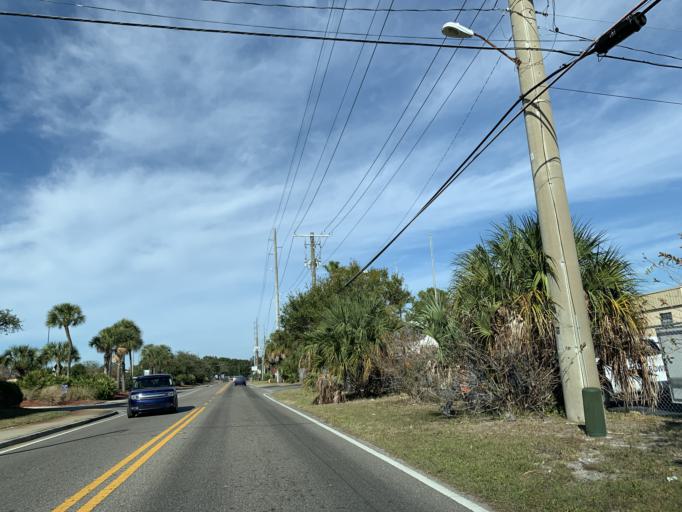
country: US
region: Florida
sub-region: Hillsborough County
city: Tampa
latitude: 27.8914
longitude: -82.5154
